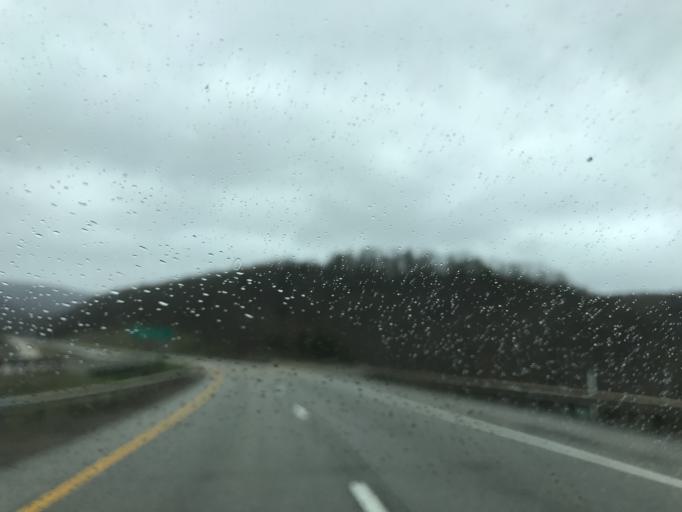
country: US
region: West Virginia
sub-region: Summers County
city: Hinton
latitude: 37.8086
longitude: -80.8152
